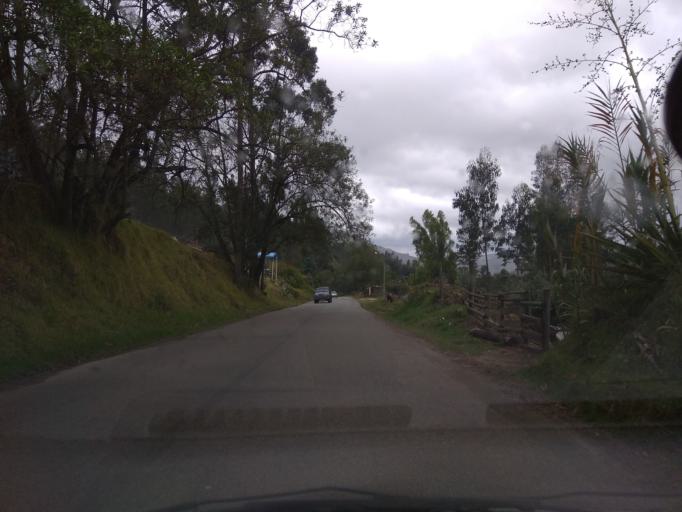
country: CO
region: Boyaca
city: Topaga
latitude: 5.7638
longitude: -72.8520
